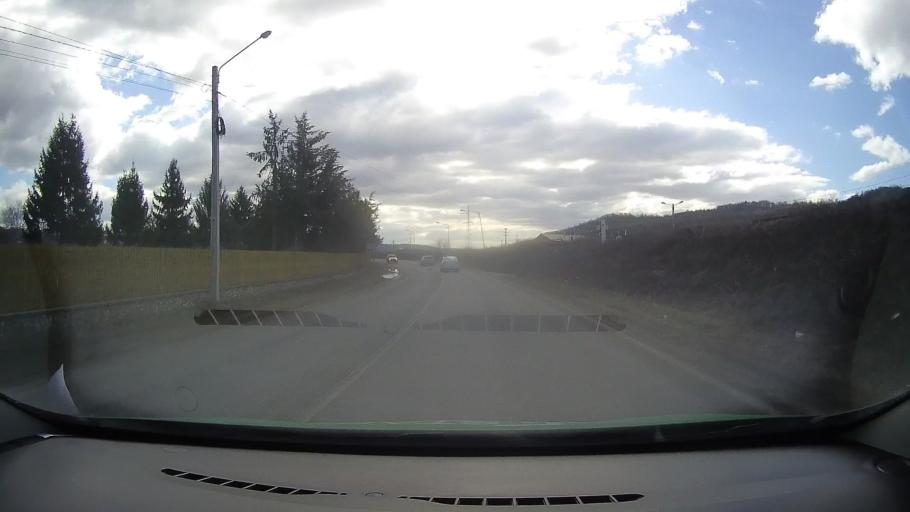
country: RO
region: Dambovita
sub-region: Oras Pucioasa
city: Pucioasa
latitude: 45.0848
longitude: 25.4214
